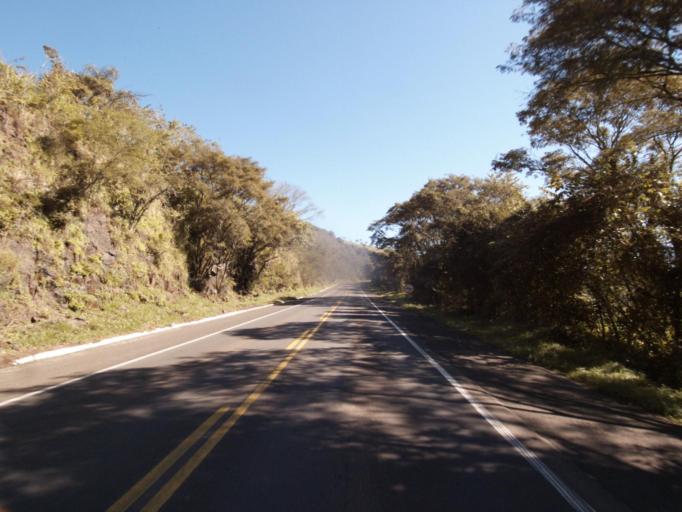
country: BR
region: Rio Grande do Sul
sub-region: Frederico Westphalen
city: Frederico Westphalen
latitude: -26.8255
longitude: -53.4011
